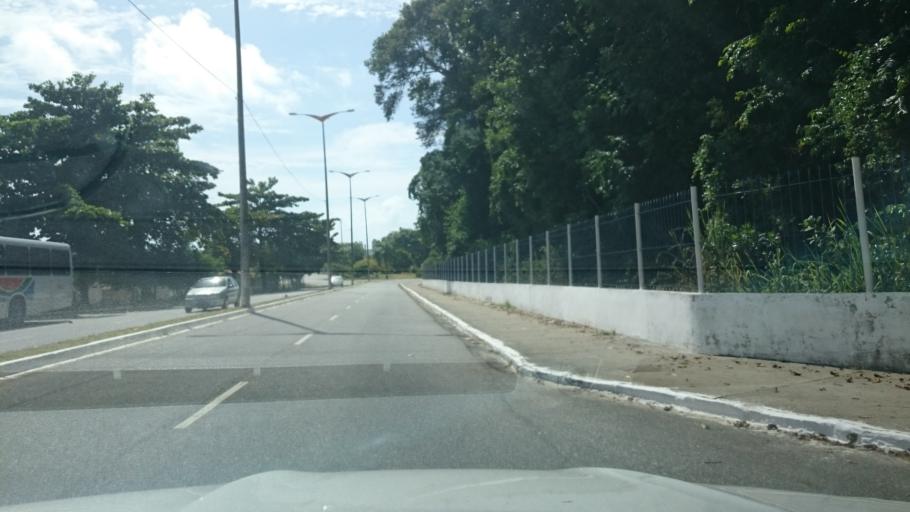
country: BR
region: Paraiba
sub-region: Joao Pessoa
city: Joao Pessoa
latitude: -7.1335
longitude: -34.8476
